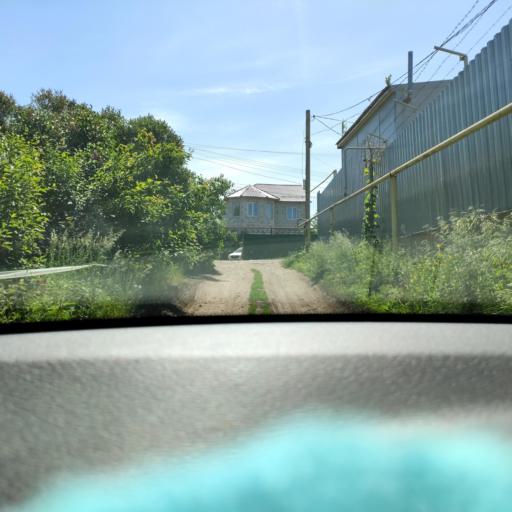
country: RU
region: Samara
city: Petra-Dubrava
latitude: 53.2883
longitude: 50.2984
